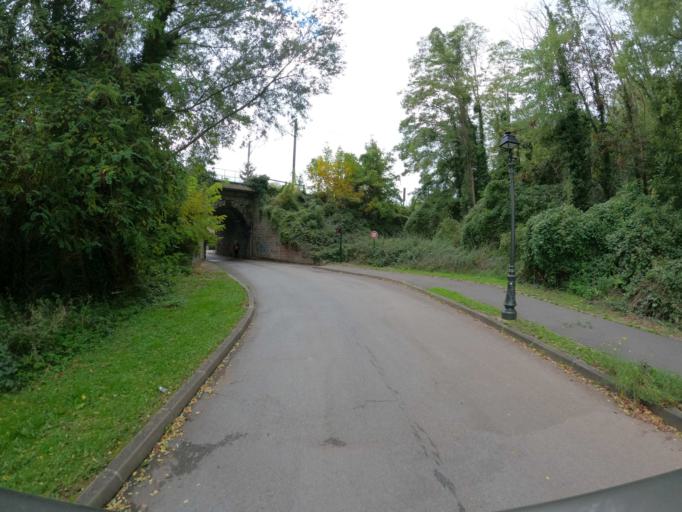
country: FR
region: Ile-de-France
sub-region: Departement de Seine-et-Marne
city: Coupvray
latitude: 48.9001
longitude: 2.7969
